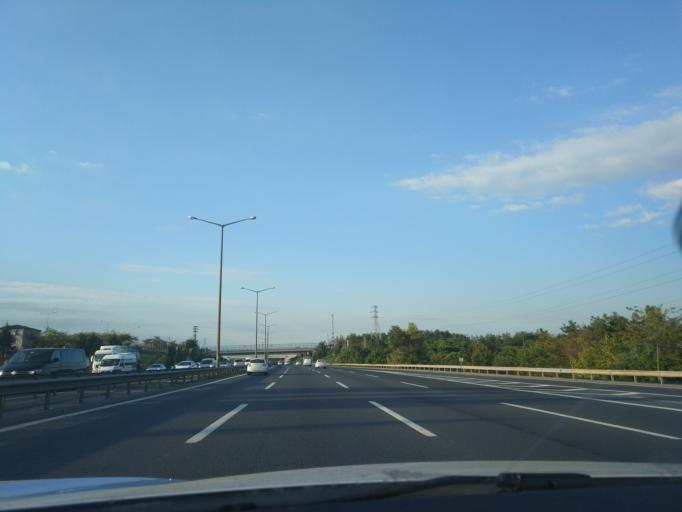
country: TR
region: Istanbul
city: Umraniye
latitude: 41.0498
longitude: 29.1212
